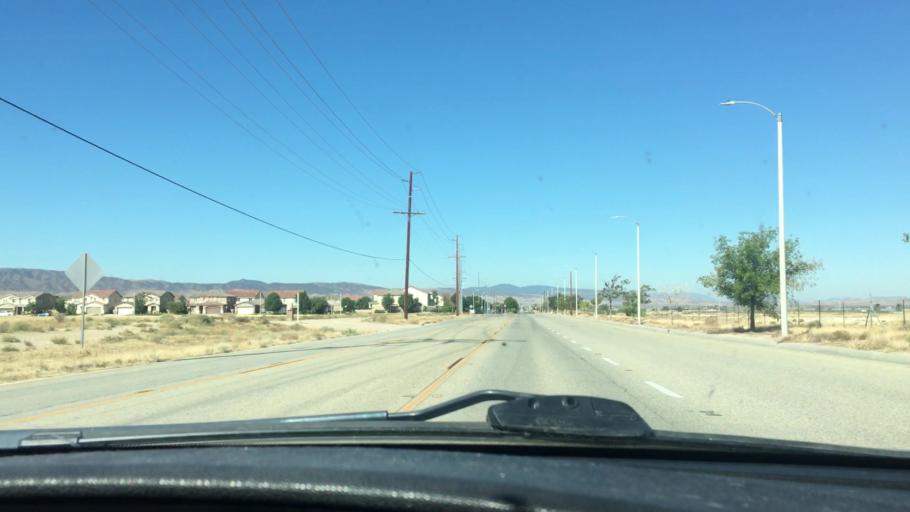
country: US
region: California
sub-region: Los Angeles County
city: Quartz Hill
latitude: 34.6894
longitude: -118.2293
